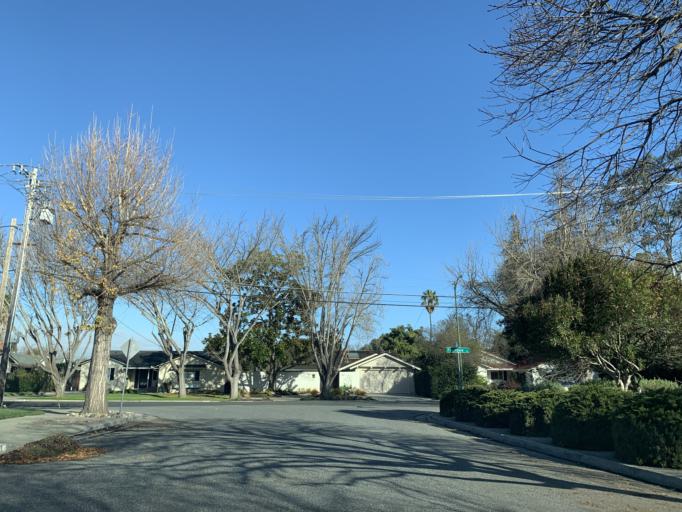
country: US
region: California
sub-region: Santa Clara County
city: Buena Vista
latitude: 37.3108
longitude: -121.9075
